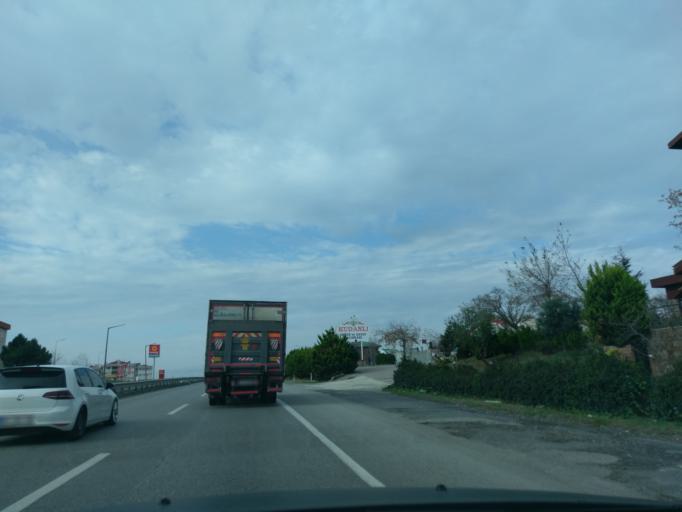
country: TR
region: Istanbul
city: Celaliye
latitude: 41.0495
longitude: 28.3939
